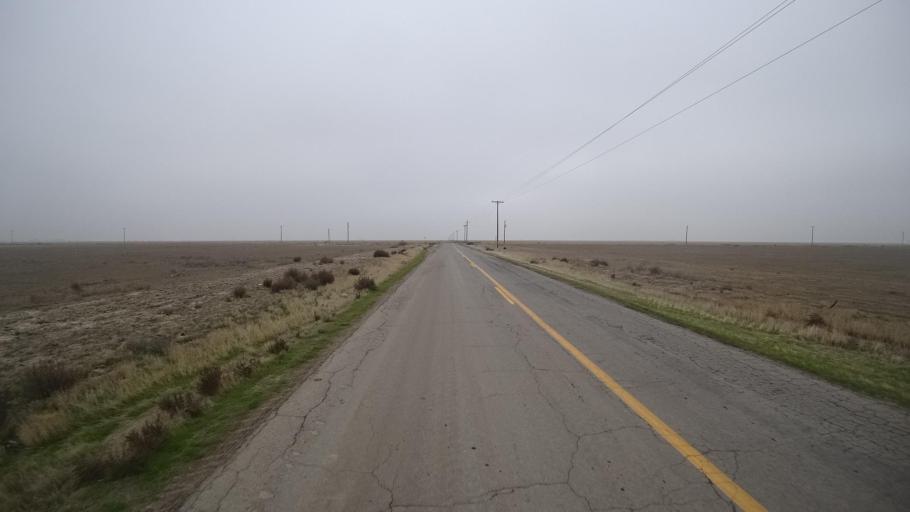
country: US
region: California
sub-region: Tulare County
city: Alpaugh
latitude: 35.7174
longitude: -119.4886
